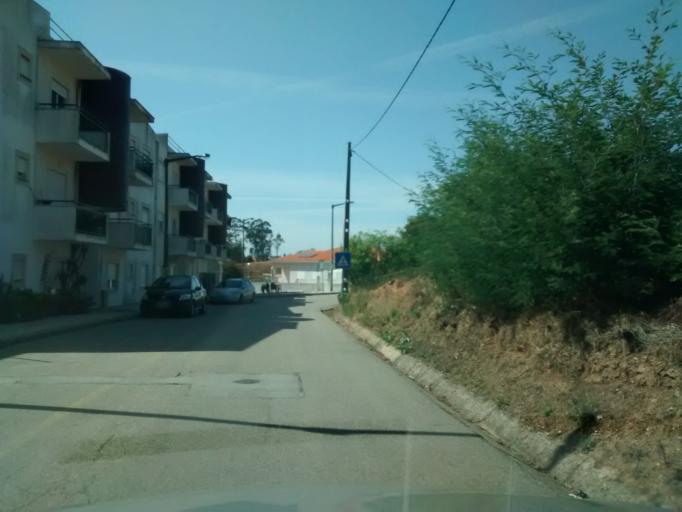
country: PT
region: Aveiro
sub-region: Mealhada
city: Mealhada
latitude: 40.3852
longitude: -8.3860
